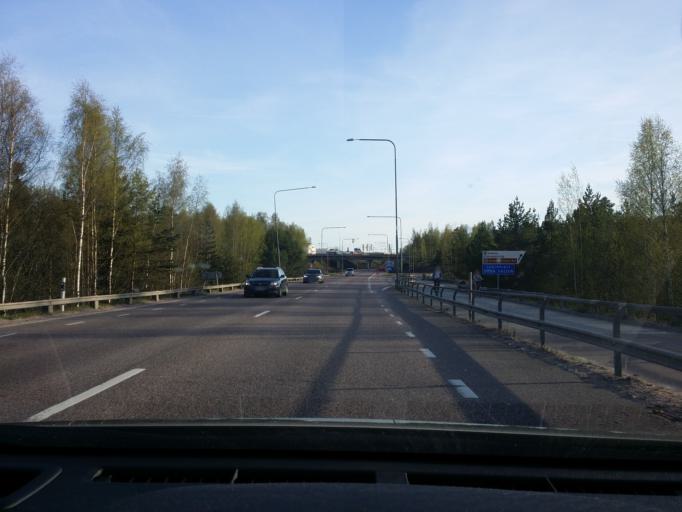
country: SE
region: Dalarna
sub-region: Avesta Kommun
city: Avesta
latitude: 60.1463
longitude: 16.1981
